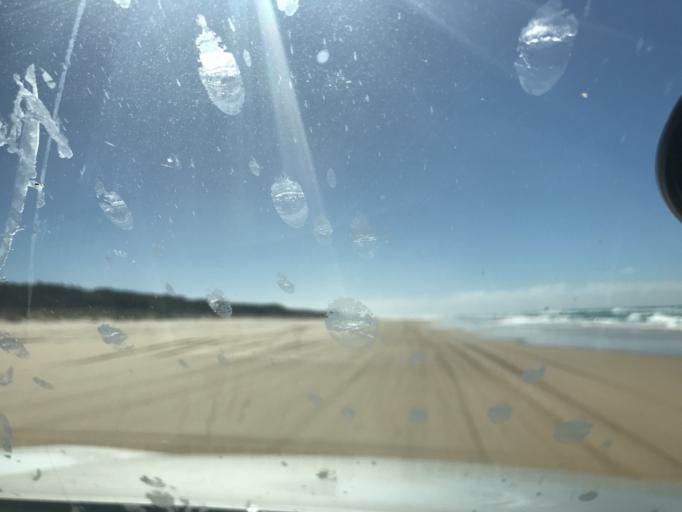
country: AU
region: Queensland
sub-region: Fraser Coast
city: Urangan
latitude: -25.0329
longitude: 153.3503
